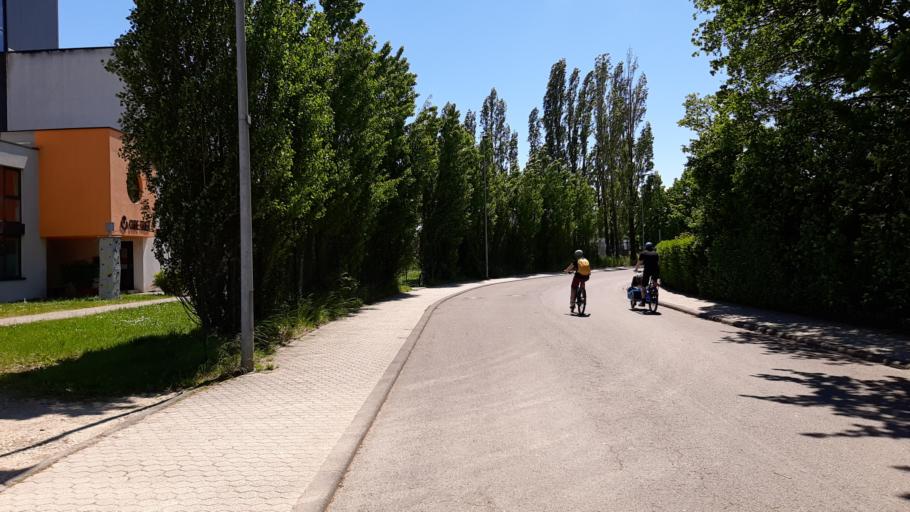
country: DE
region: Rheinland-Pfalz
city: Trier
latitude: 49.7297
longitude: 6.6151
